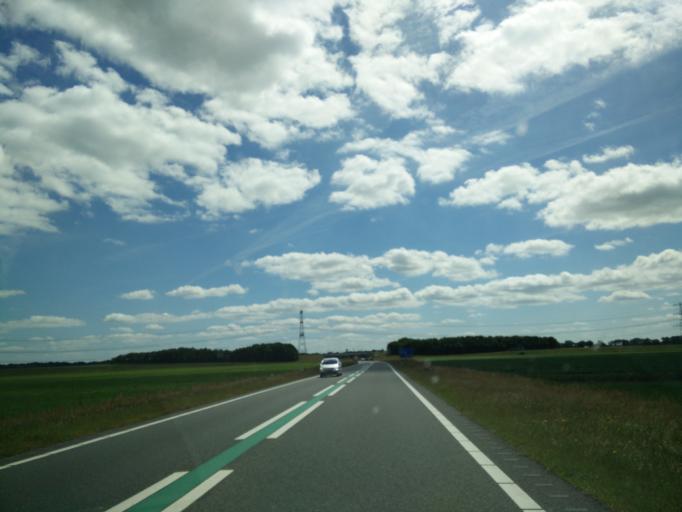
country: NL
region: Drenthe
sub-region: Gemeente Coevorden
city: Sleen
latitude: 52.7921
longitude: 6.8404
